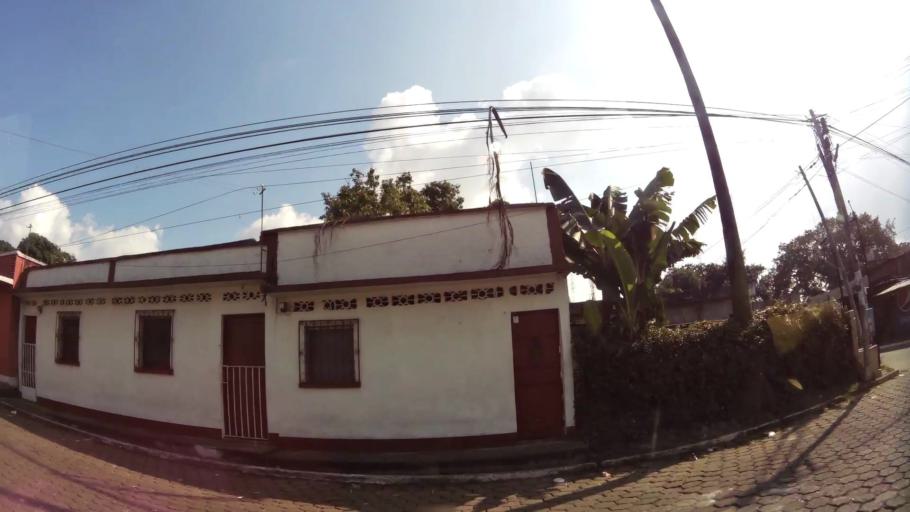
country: GT
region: Retalhuleu
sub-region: Municipio de Retalhuleu
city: Retalhuleu
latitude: 14.5444
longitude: -91.6808
